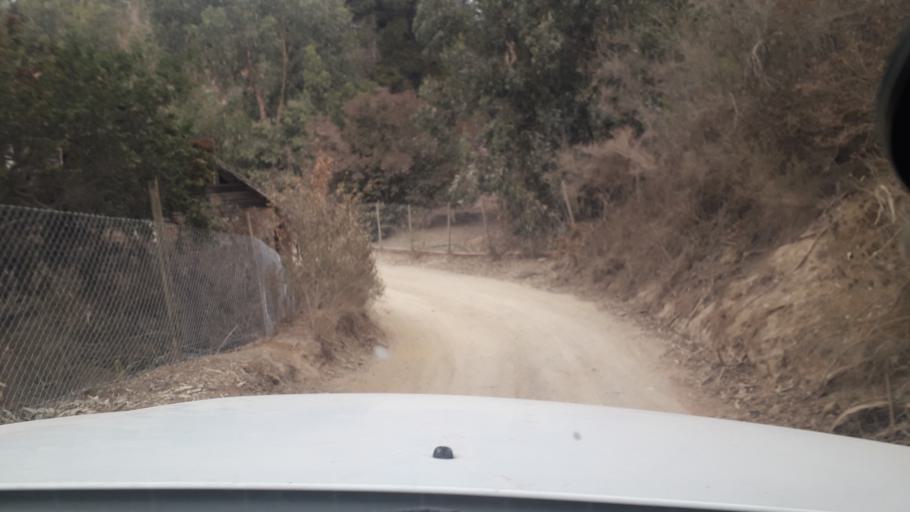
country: CL
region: Valparaiso
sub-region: Provincia de Valparaiso
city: Valparaiso
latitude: -33.1171
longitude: -71.6379
